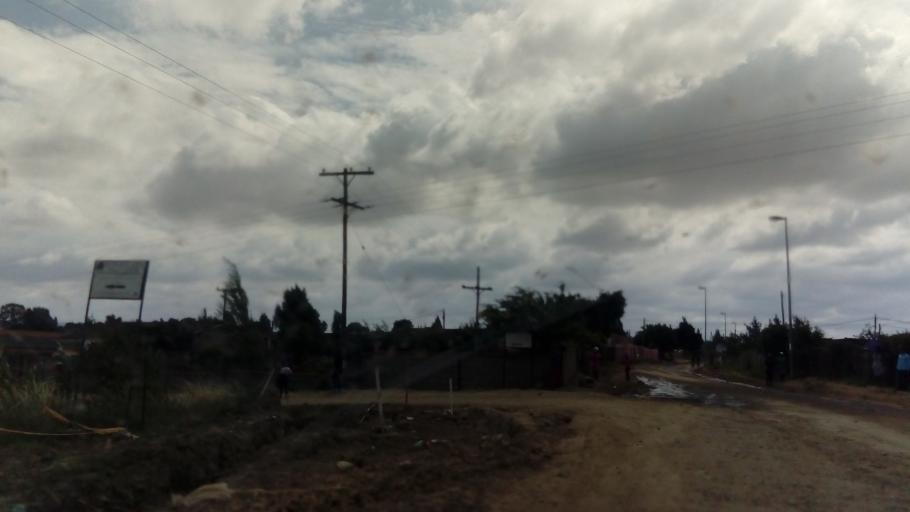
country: LS
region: Maseru
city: Maseru
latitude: -29.3705
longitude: 27.5346
